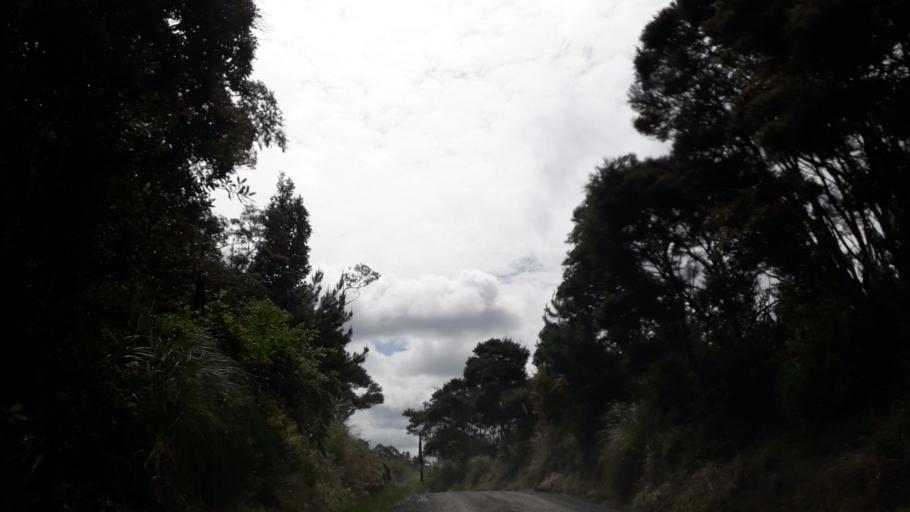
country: NZ
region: Northland
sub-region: Far North District
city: Kaitaia
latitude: -35.1984
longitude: 173.2821
